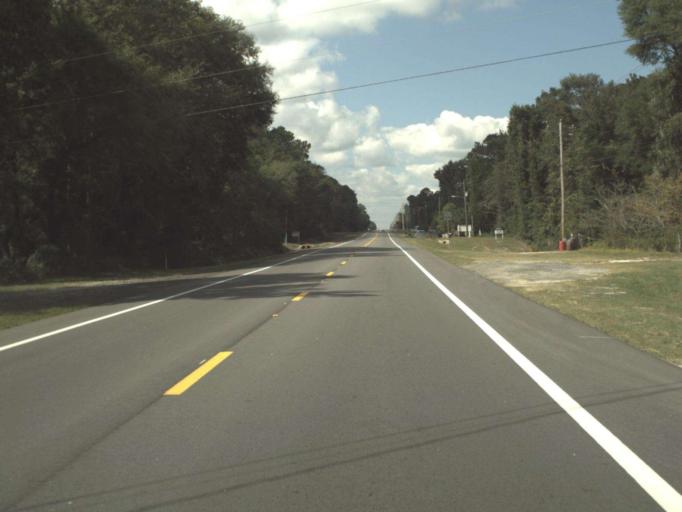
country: US
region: Florida
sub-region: Walton County
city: Freeport
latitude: 30.5035
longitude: -86.1508
